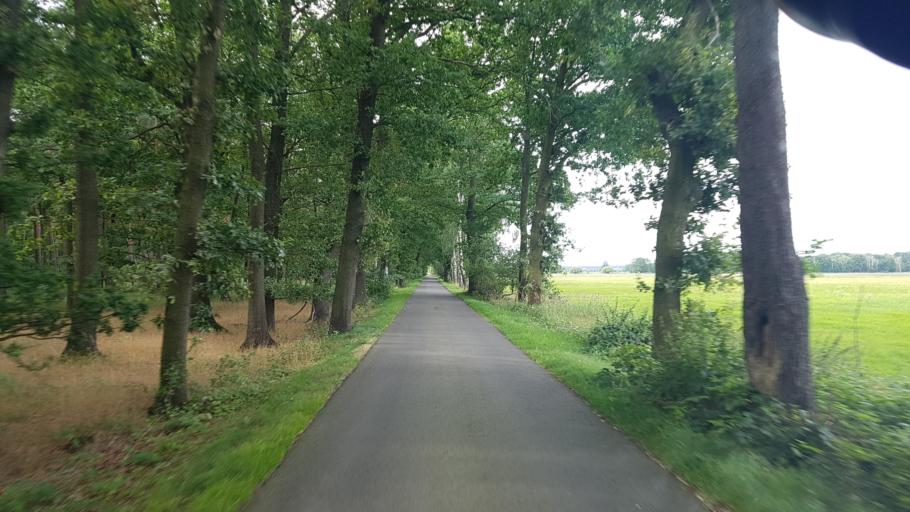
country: DE
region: Brandenburg
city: Bronkow
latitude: 51.6157
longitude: 13.9463
